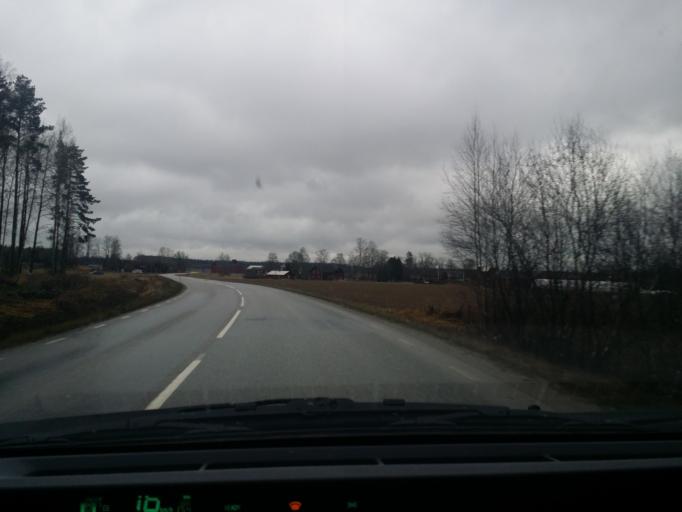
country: SE
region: Vaestmanland
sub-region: Vasteras
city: Skultuna
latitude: 59.7971
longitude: 16.5169
